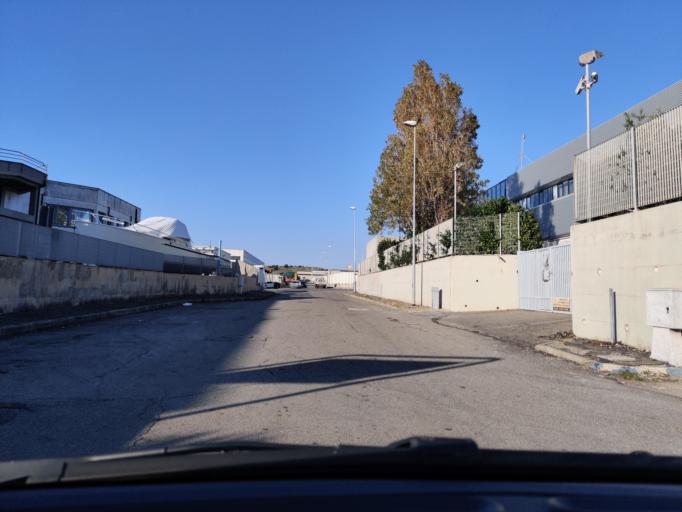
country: IT
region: Latium
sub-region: Citta metropolitana di Roma Capitale
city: Aurelia
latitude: 42.1196
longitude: 11.7807
